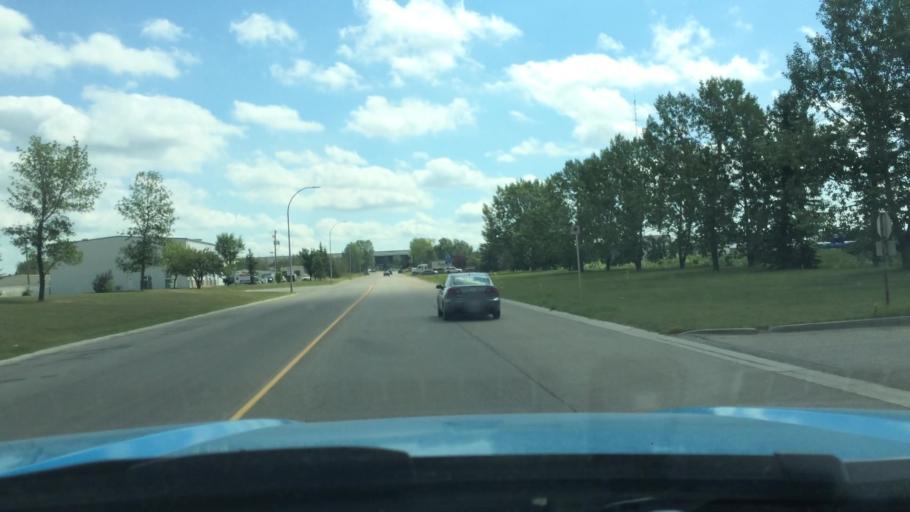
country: CA
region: Alberta
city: Airdrie
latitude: 51.2889
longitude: -113.9892
